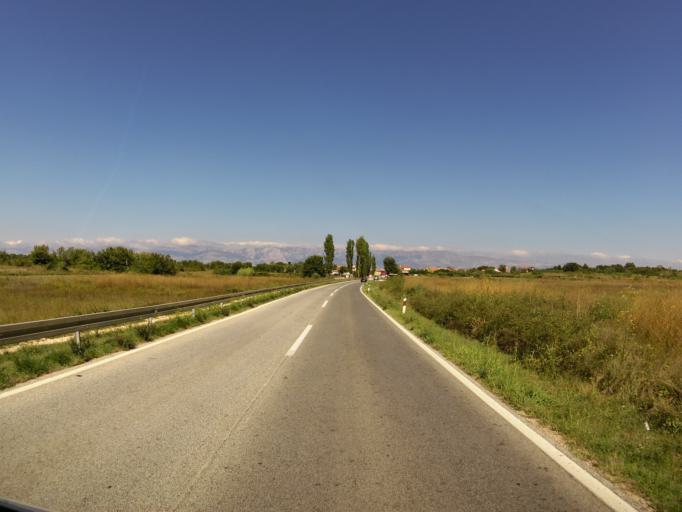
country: HR
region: Zadarska
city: Policnik
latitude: 44.1835
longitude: 15.3939
